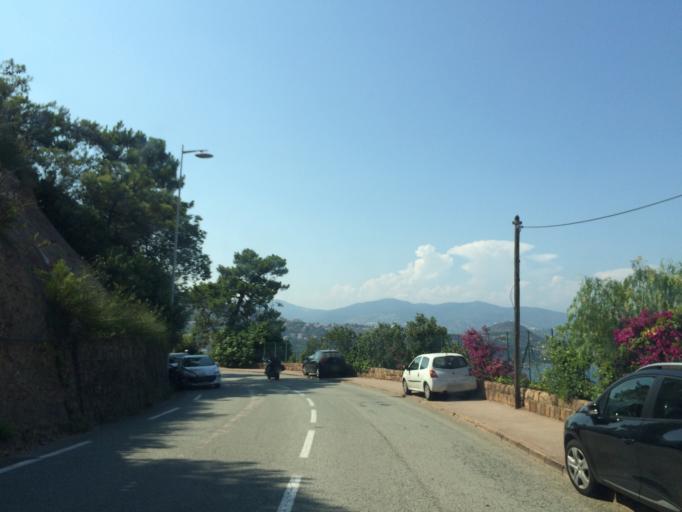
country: FR
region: Provence-Alpes-Cote d'Azur
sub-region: Departement des Alpes-Maritimes
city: Theoule-sur-Mer
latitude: 43.5050
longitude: 6.9485
